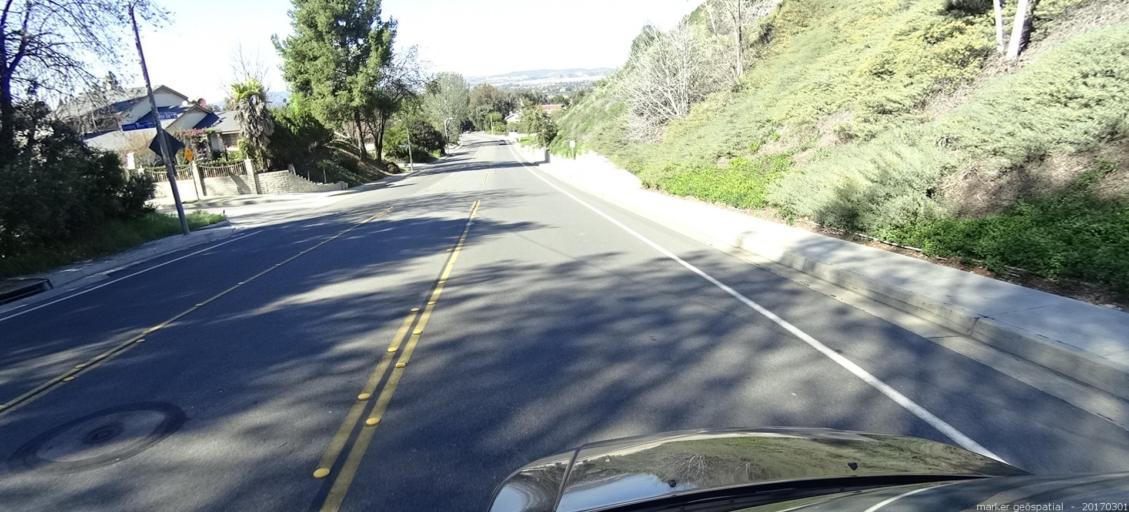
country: US
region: California
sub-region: Orange County
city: Villa Park
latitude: 33.8469
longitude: -117.8011
